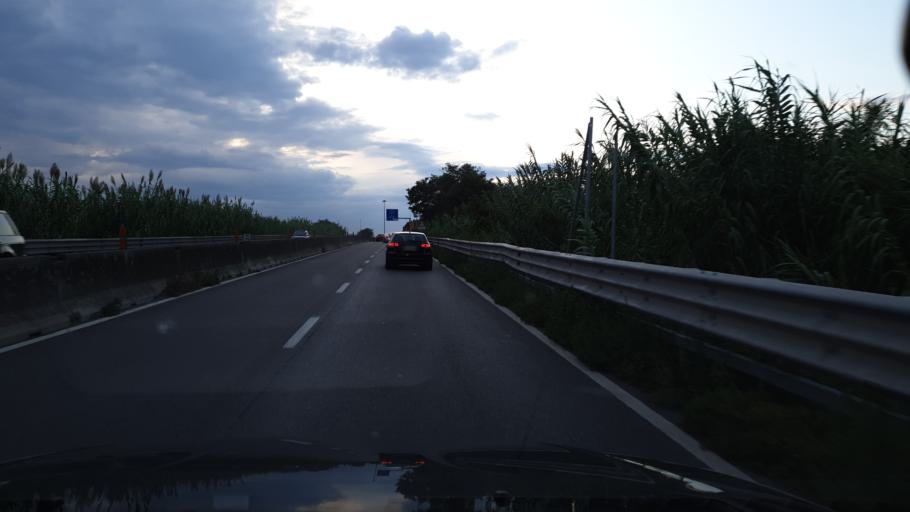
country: IT
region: Emilia-Romagna
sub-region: Provincia di Ravenna
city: Madonna Dell'Albero
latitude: 44.3833
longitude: 12.1988
